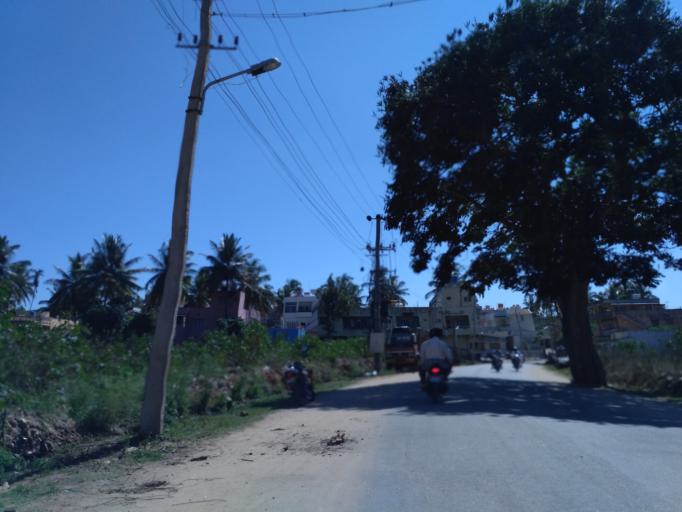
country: IN
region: Karnataka
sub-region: Hassan
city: Hassan
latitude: 13.0155
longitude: 76.0945
